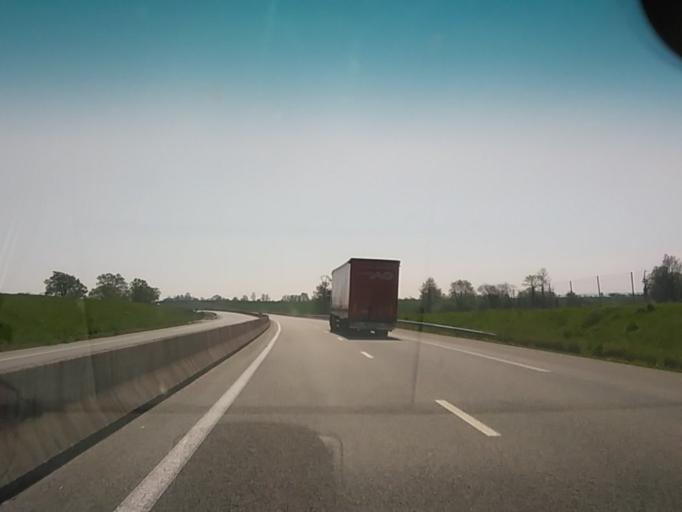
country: FR
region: Lower Normandy
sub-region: Departement de l'Orne
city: Mortree
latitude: 48.6667
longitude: 0.0618
